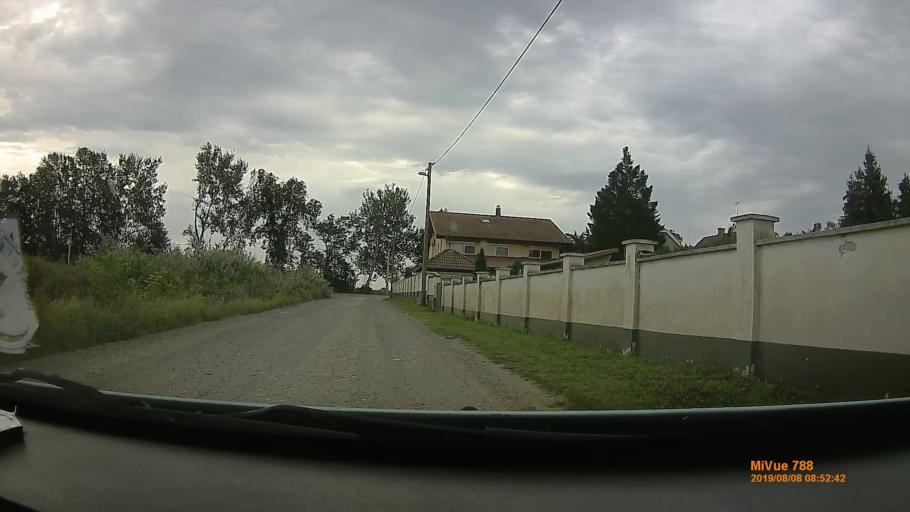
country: HU
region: Hajdu-Bihar
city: Debrecen
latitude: 47.5986
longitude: 21.6470
